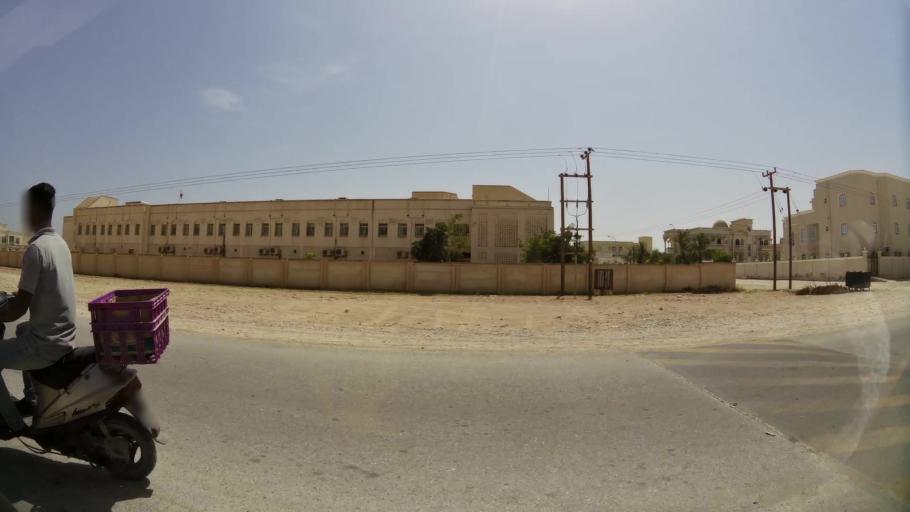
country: OM
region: Zufar
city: Salalah
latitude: 17.0444
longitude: 54.1546
